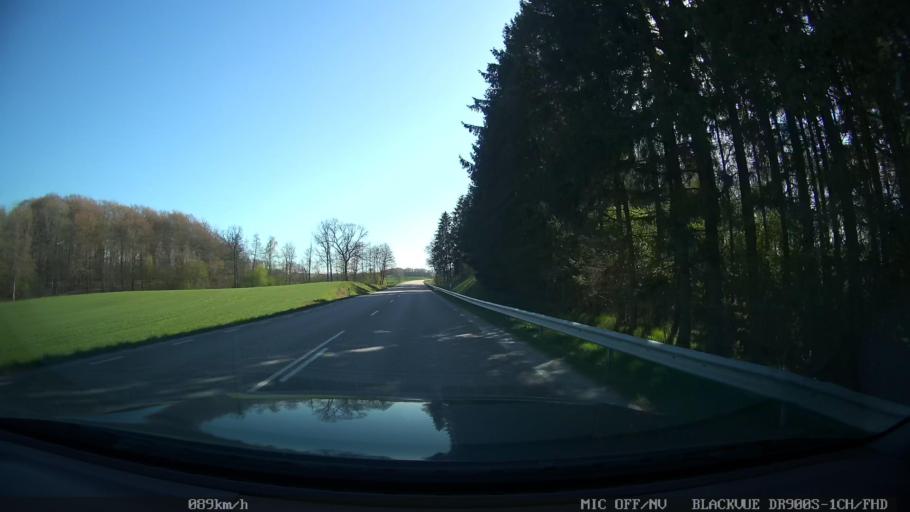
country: SE
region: Skane
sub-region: Klippans Kommun
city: Ljungbyhed
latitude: 55.9818
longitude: 13.2713
